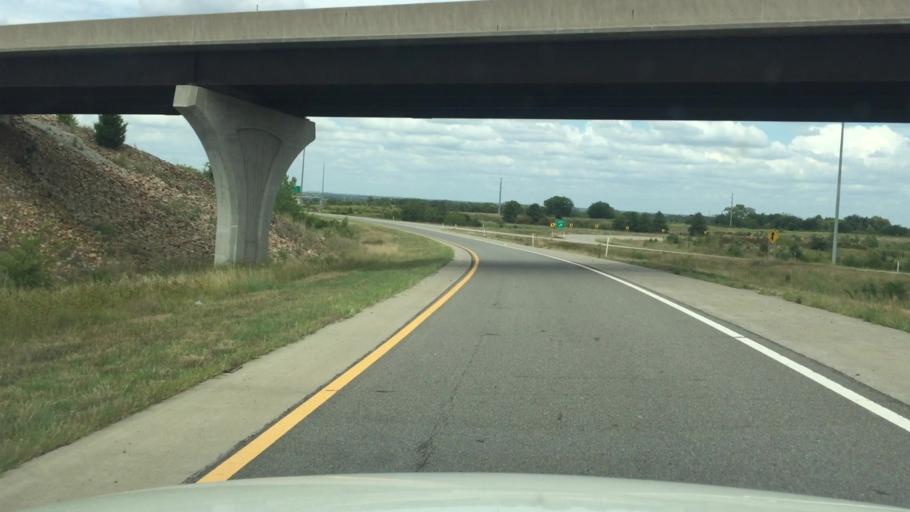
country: US
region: Kansas
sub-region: Shawnee County
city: Topeka
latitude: 39.0359
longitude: -95.6070
